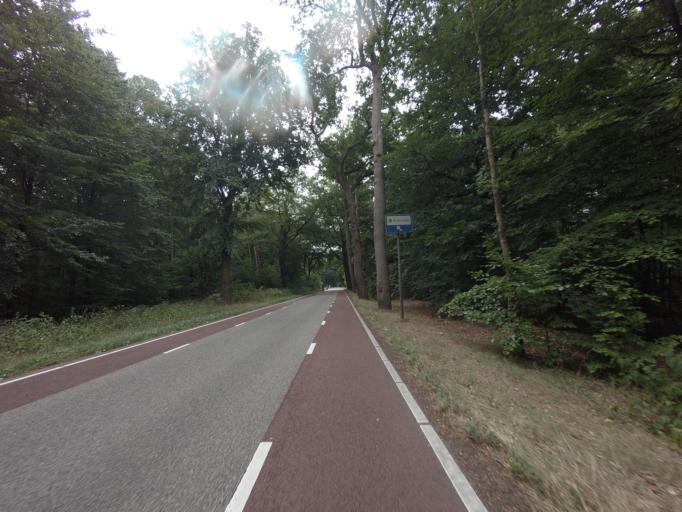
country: NL
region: Gelderland
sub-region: Gemeente Arnhem
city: Gulden Bodem
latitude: 52.0168
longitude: 5.8938
